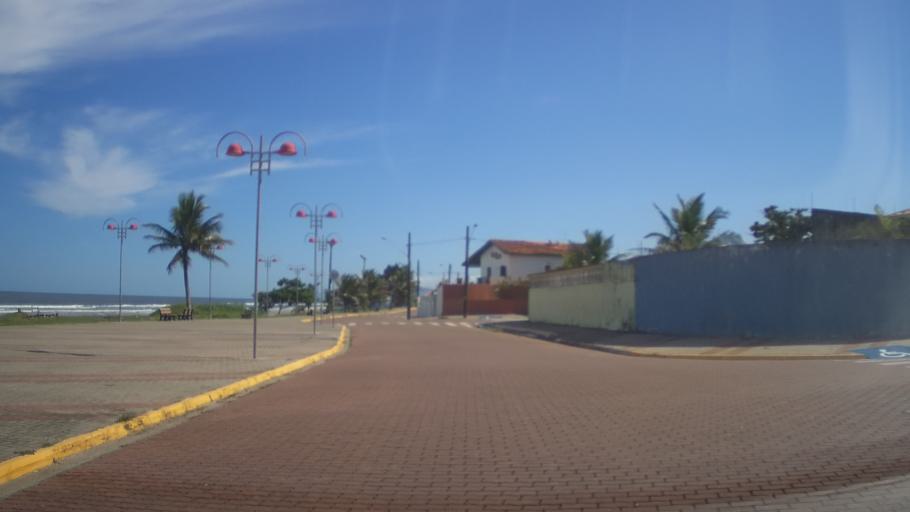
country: BR
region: Sao Paulo
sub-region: Itanhaem
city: Itanhaem
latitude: -24.1731
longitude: -46.7633
